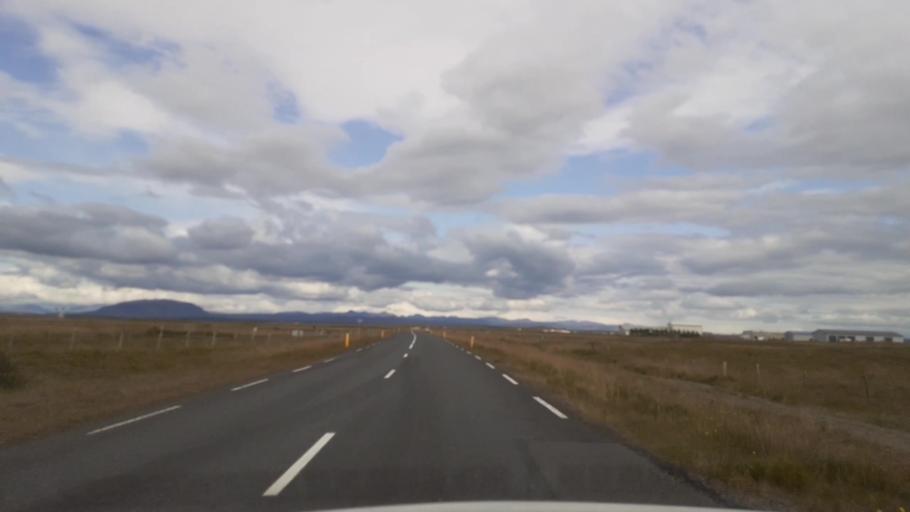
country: IS
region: South
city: Selfoss
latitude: 63.9412
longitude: -20.8385
